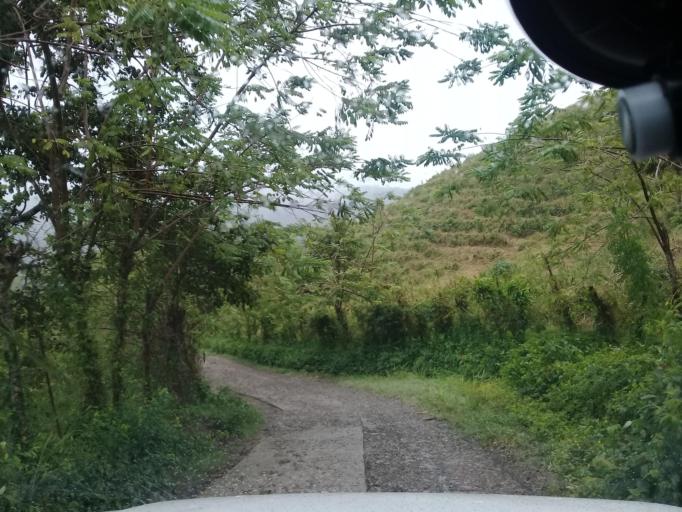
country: MX
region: Veracruz
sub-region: Chalma
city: San Pedro Coyutla
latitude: 21.2299
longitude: -98.4500
